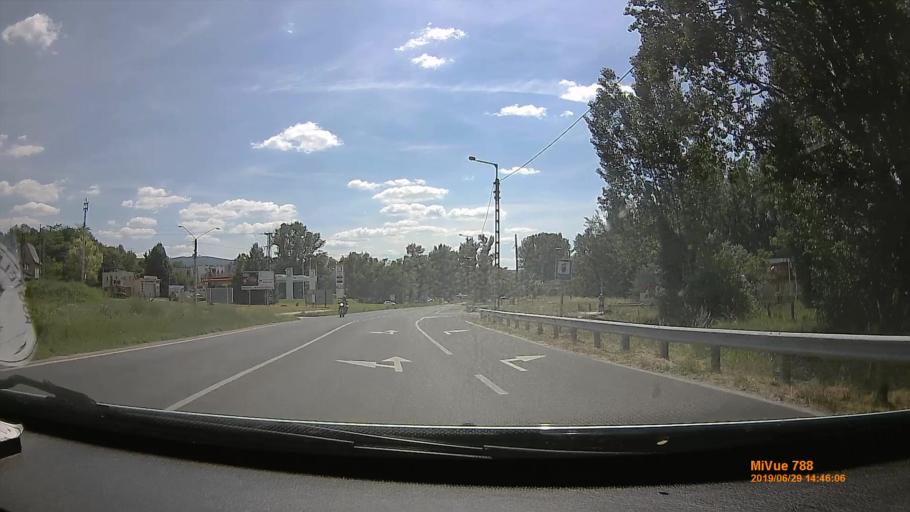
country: HU
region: Komarom-Esztergom
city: Nyergesujfalu
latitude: 47.7577
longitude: 18.5337
